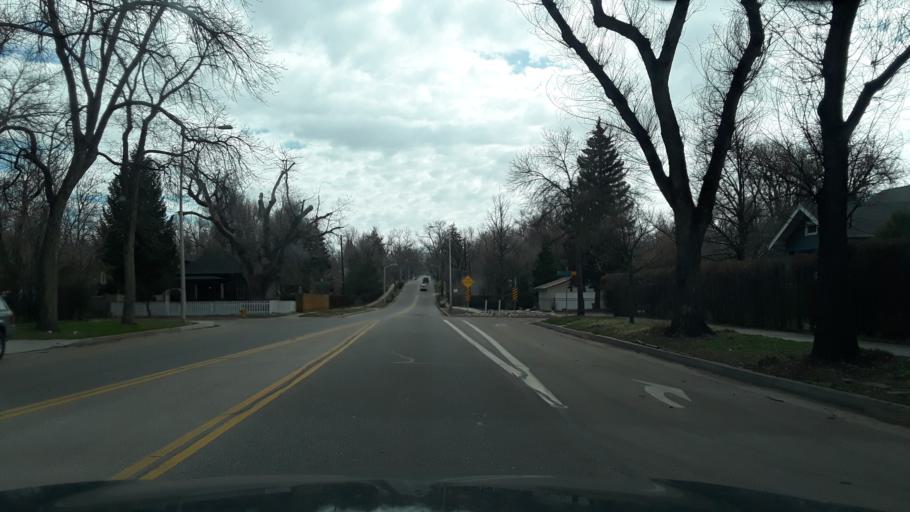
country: US
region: Colorado
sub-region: El Paso County
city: Colorado Springs
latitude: 38.8502
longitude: -104.8107
